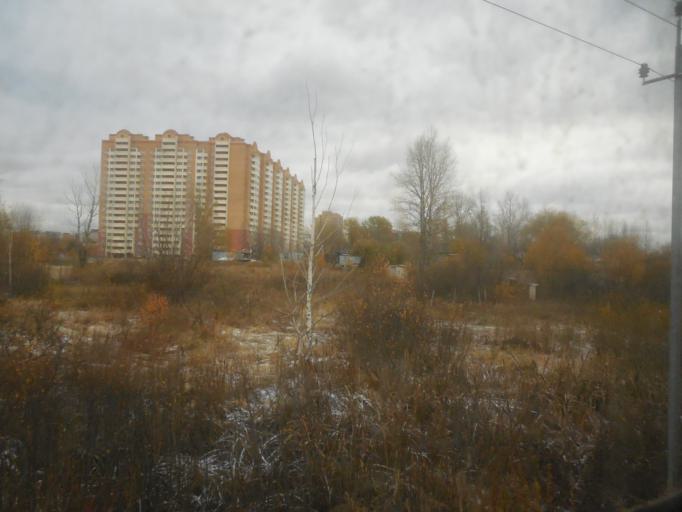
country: RU
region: Moskovskaya
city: Bol'shiye Vyazemy
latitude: 55.6223
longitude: 36.9743
